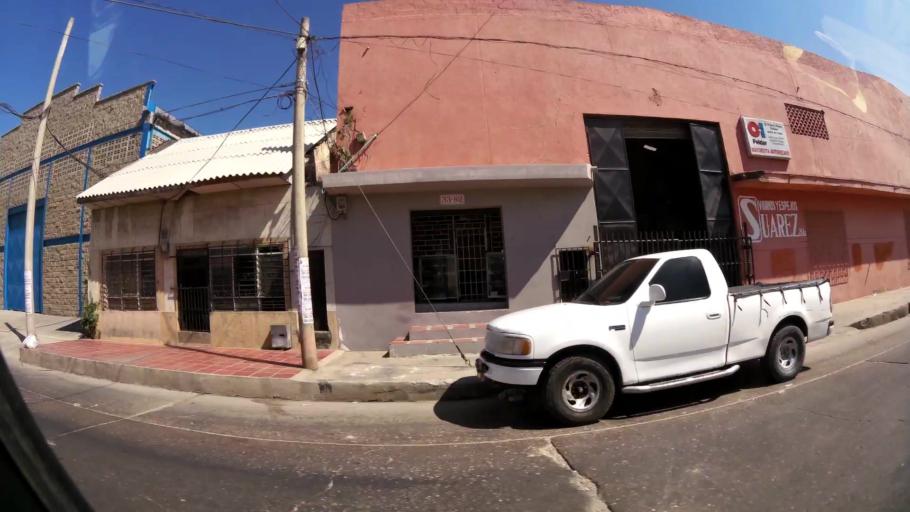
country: CO
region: Atlantico
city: Barranquilla
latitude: 10.9739
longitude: -74.7830
